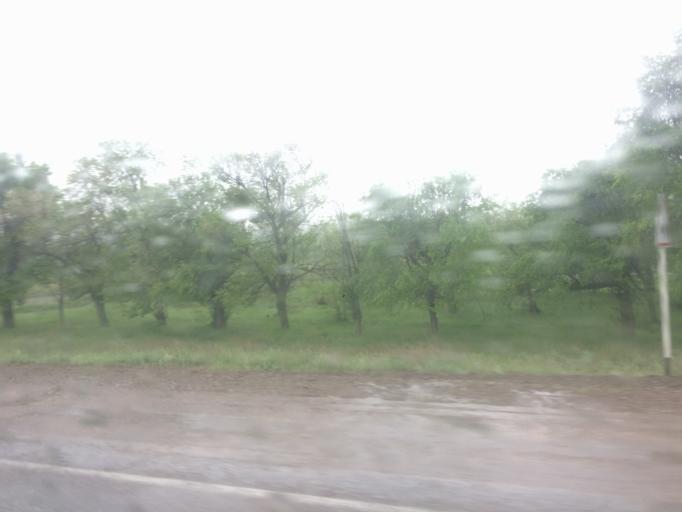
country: KZ
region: Zhambyl
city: Georgiyevka
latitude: 43.2034
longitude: 74.7282
